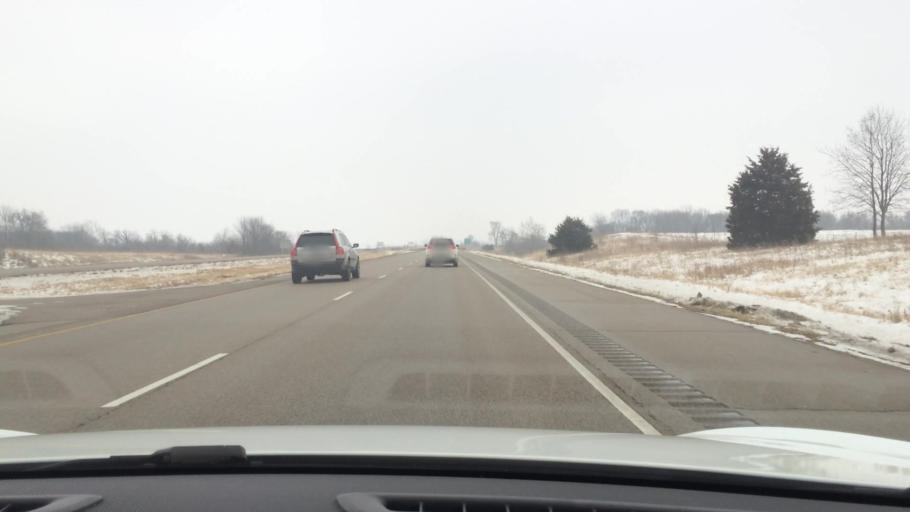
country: US
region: Illinois
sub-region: McLean County
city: Le Roy
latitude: 40.3299
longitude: -88.7488
